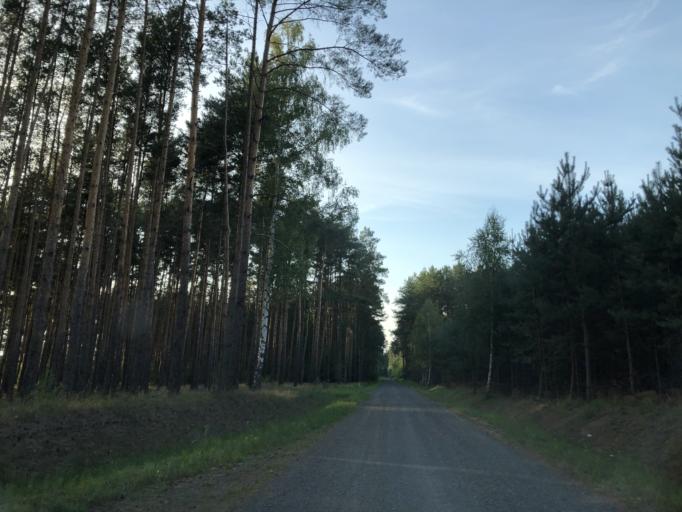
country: PL
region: Lubusz
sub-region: Powiat swiebodzinski
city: Zbaszynek
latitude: 52.2297
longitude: 15.7938
